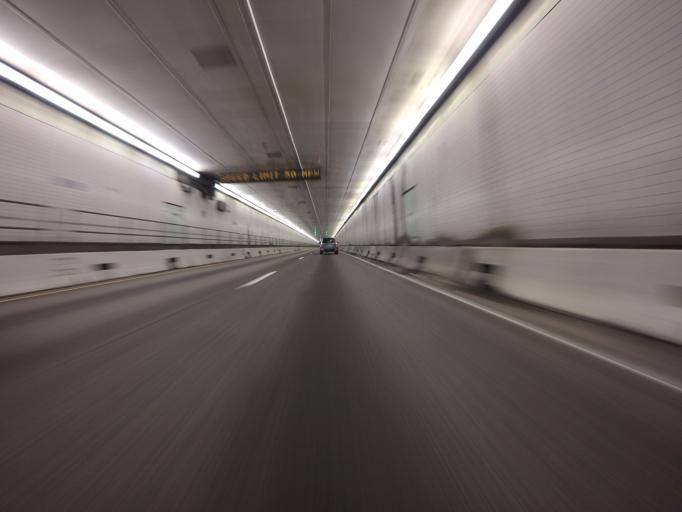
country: US
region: Colorado
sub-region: Summit County
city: Keystone
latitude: 39.6783
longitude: -105.9074
